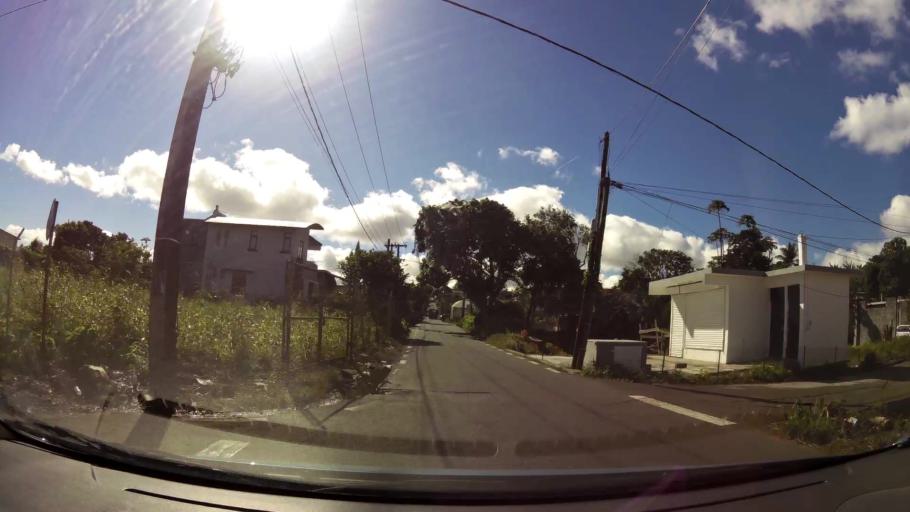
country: MU
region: Plaines Wilhems
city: Vacoas
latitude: -20.3028
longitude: 57.5003
